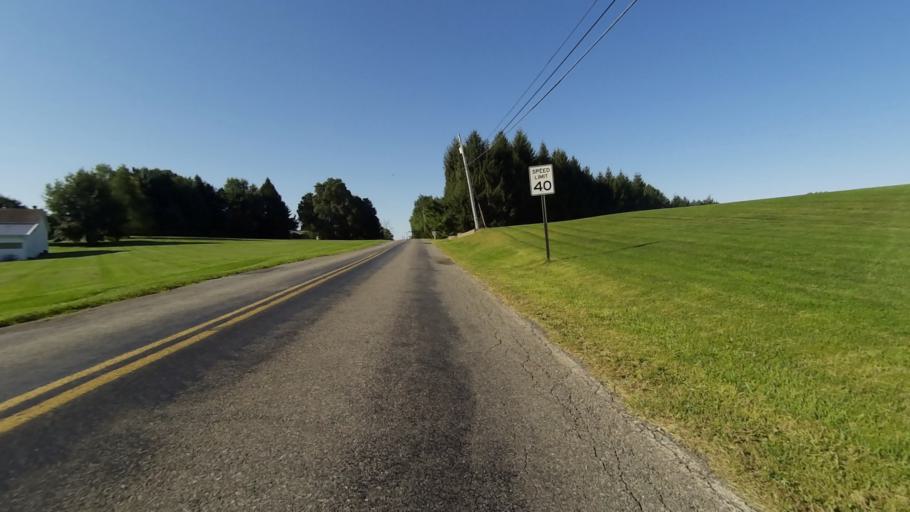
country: US
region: Ohio
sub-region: Portage County
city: Mantua
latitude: 41.2905
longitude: -81.2634
